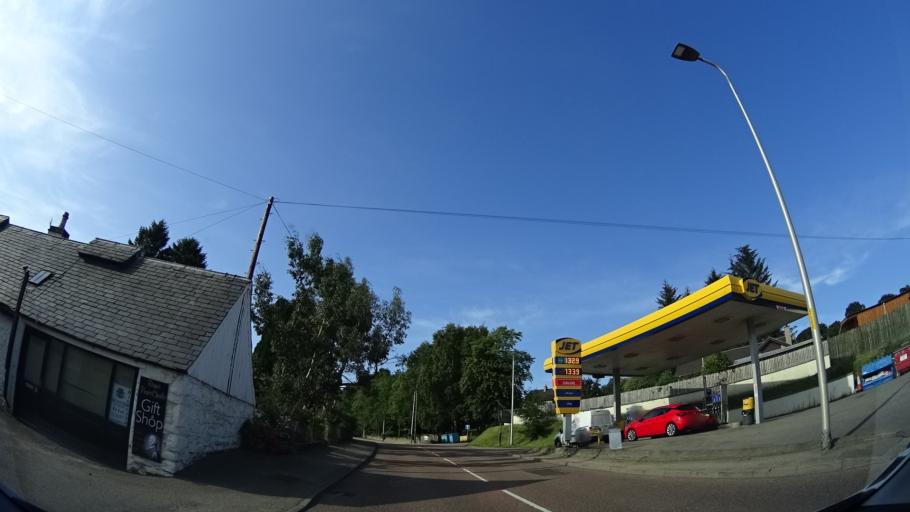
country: GB
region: Scotland
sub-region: Highland
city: Muir of Ord
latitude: 57.5674
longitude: -4.5790
